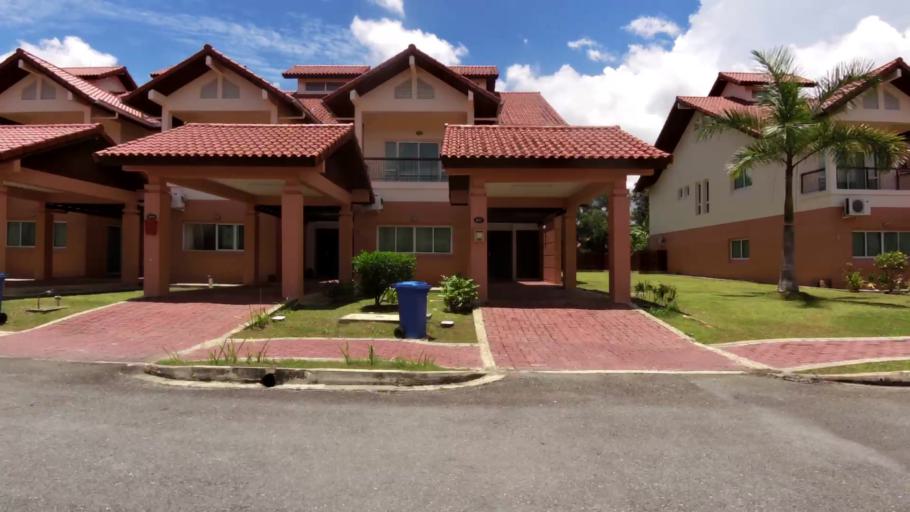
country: BN
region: Brunei and Muara
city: Bandar Seri Begawan
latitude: 4.9542
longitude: 114.8913
